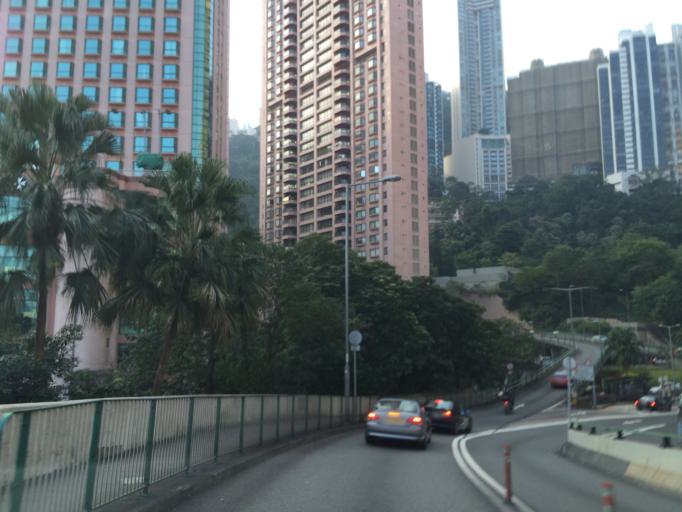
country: HK
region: Central and Western
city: Central
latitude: 22.2768
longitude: 114.1550
